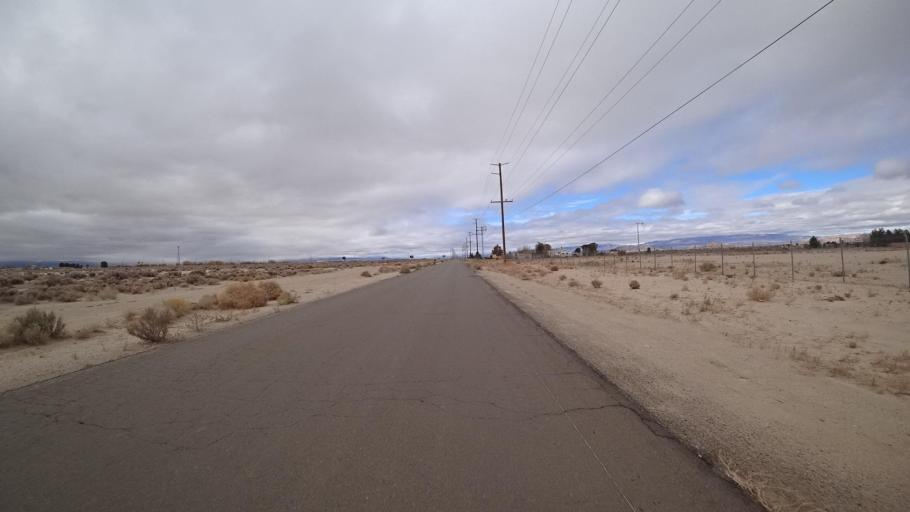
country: US
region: California
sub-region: Kern County
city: Rosamond
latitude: 34.8354
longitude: -118.1612
